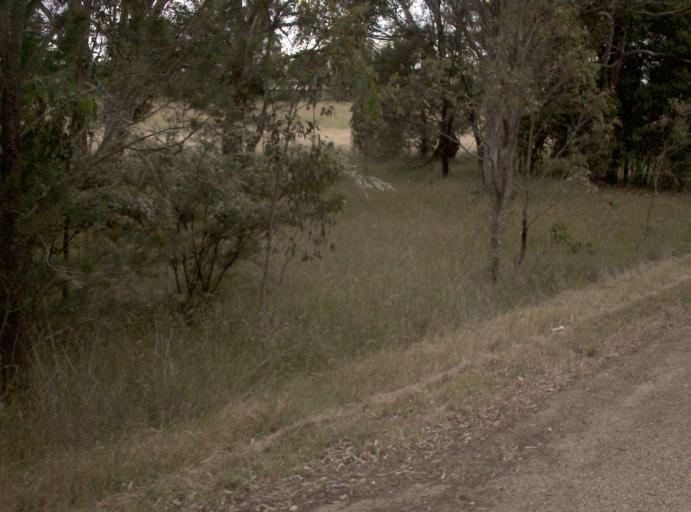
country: AU
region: Victoria
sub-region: Wellington
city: Sale
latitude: -38.0015
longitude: 147.3178
